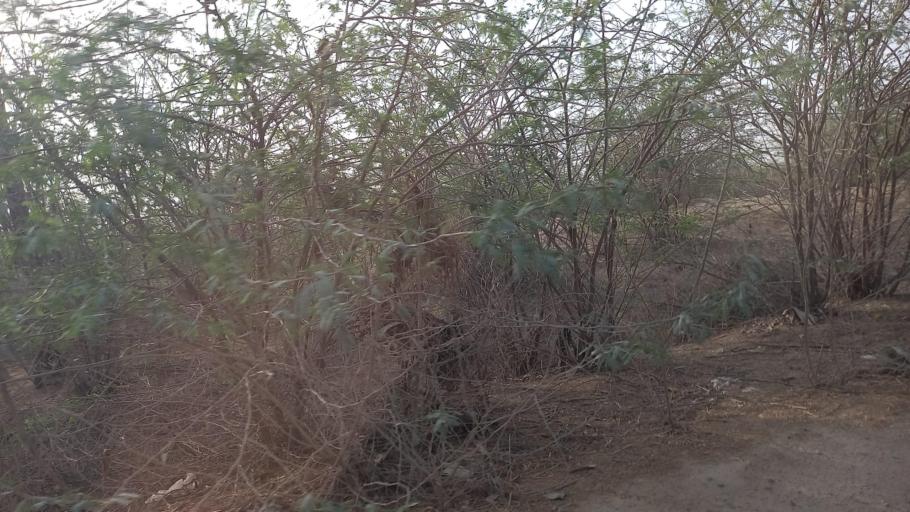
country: PK
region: Sindh
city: Malir Cantonment
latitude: 25.1135
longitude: 67.1915
